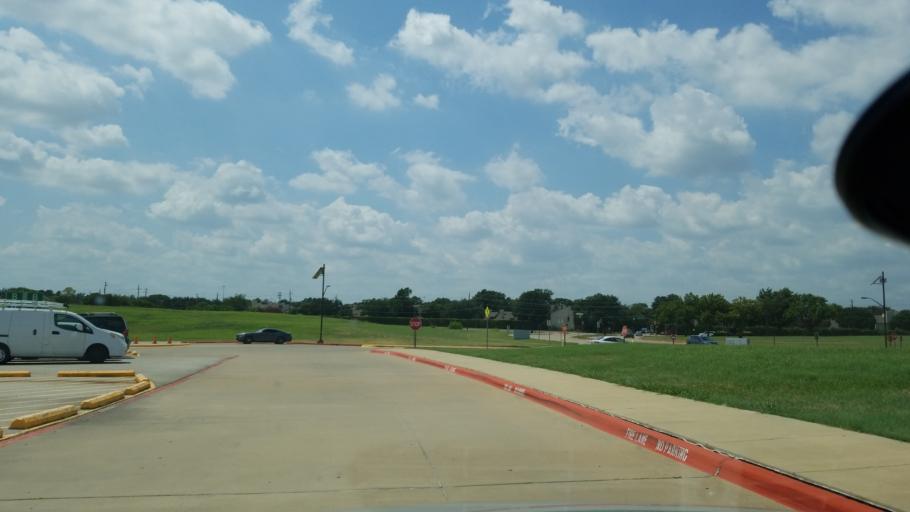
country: US
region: Texas
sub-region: Dallas County
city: Richardson
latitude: 32.9211
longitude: -96.7330
